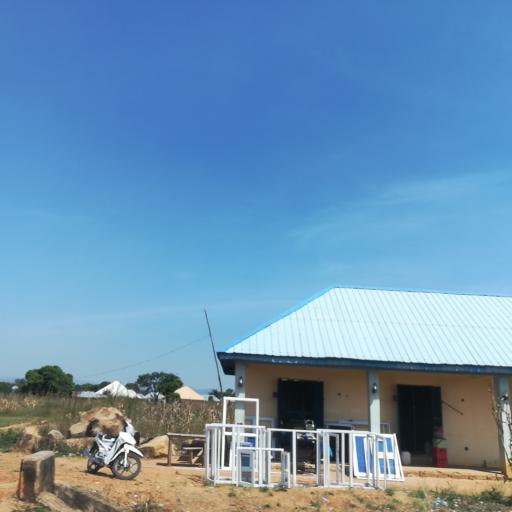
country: NG
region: Plateau
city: Jos
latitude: 9.8591
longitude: 8.9302
